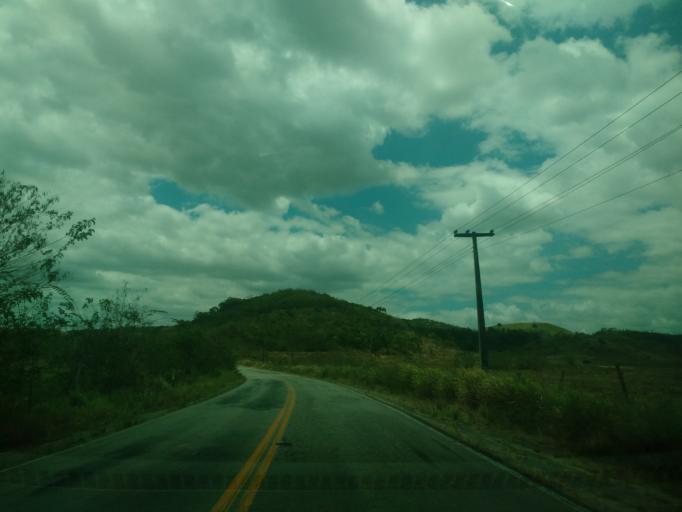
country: BR
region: Alagoas
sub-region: Uniao Dos Palmares
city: Uniao dos Palmares
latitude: -9.1385
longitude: -36.1032
